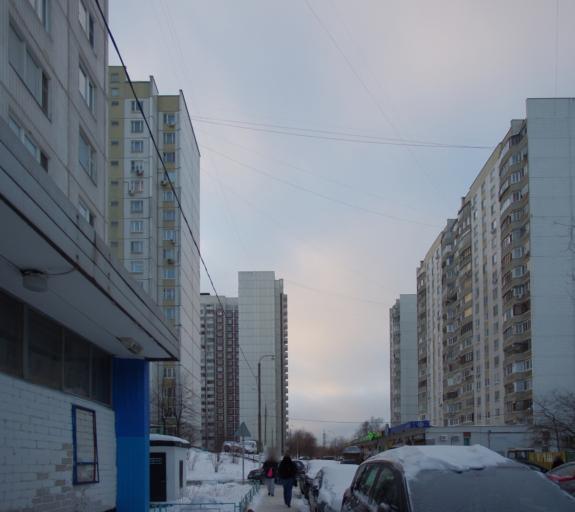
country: RU
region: Moscow
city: Tsaritsyno
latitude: 55.6404
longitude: 37.6594
